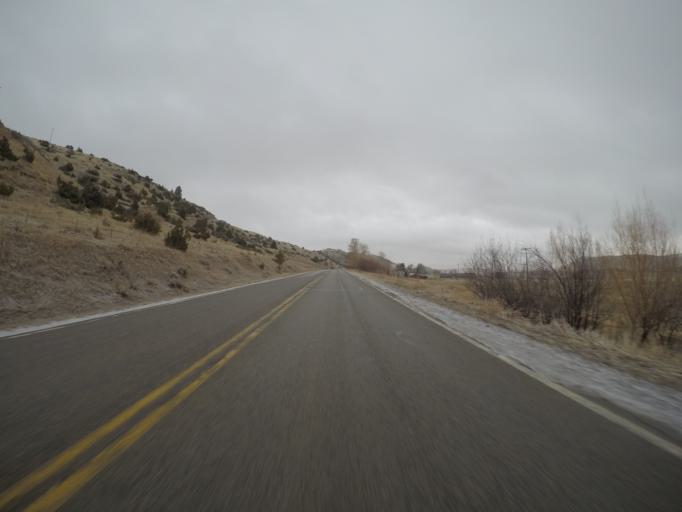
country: US
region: Montana
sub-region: Stillwater County
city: Absarokee
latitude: 45.5237
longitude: -109.4500
